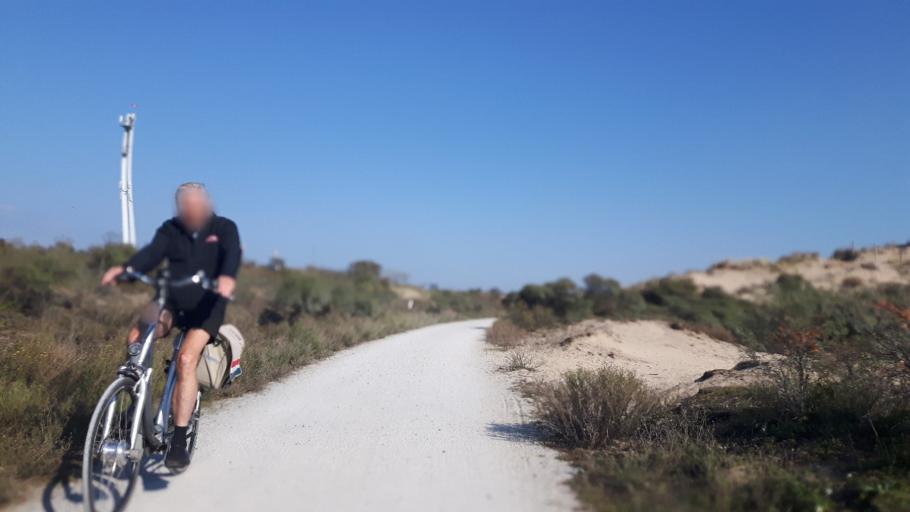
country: NL
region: South Holland
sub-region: Gemeente Noordwijkerhout
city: Noordwijkerhout
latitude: 52.2903
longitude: 4.4735
